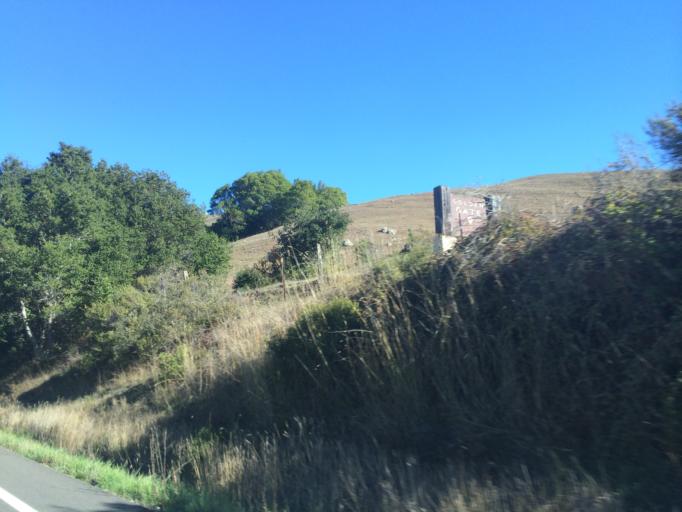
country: US
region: California
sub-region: Marin County
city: Lagunitas-Forest Knolls
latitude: 38.0408
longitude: -122.7450
